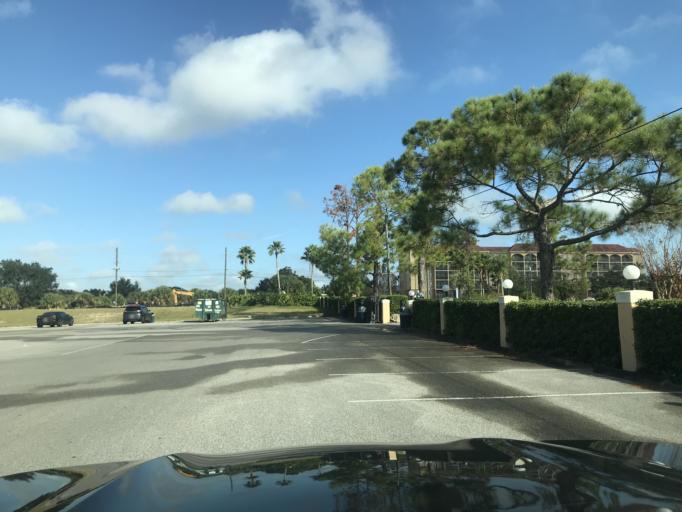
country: US
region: Florida
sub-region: Polk County
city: Citrus Ridge
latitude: 28.3315
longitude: -81.5929
